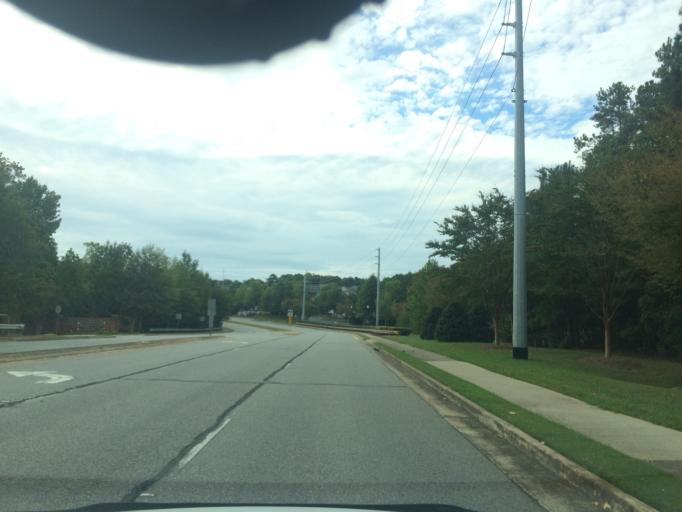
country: US
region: Georgia
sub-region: Cobb County
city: Kennesaw
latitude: 34.0541
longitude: -84.5875
